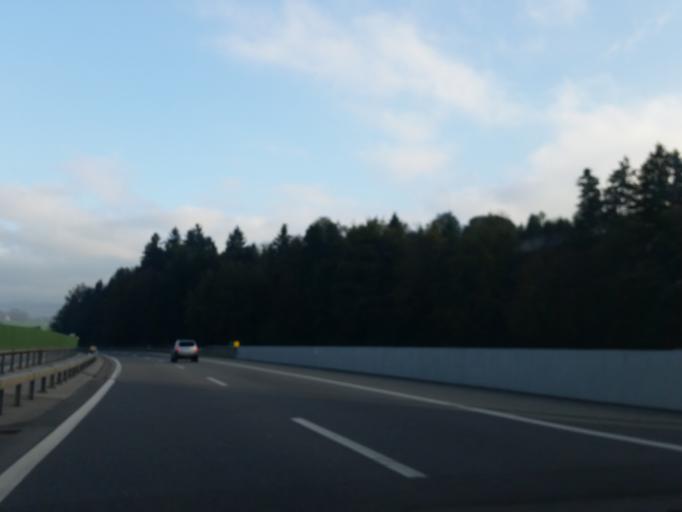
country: CH
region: Zurich
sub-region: Bezirk Affoltern
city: Knonau
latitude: 47.2086
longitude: 8.4705
